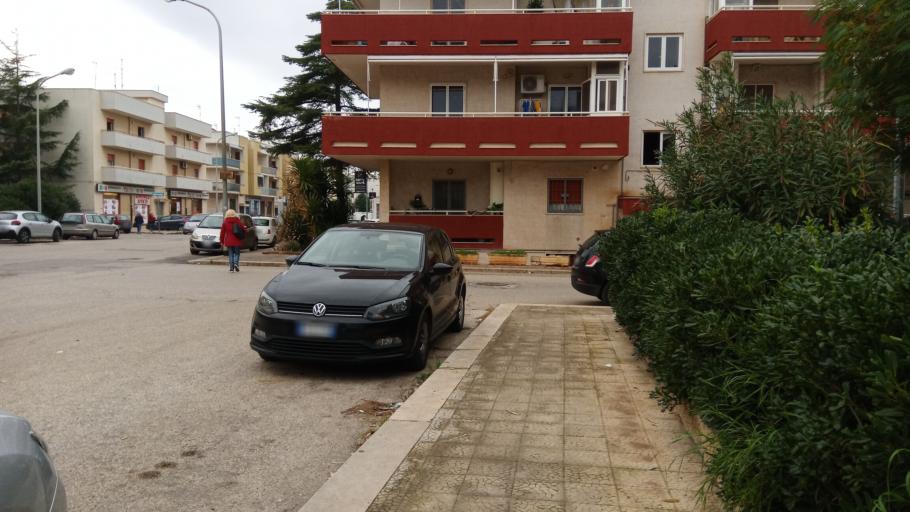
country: IT
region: Apulia
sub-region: Provincia di Bari
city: Polignano a Mare
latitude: 40.9896
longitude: 17.2268
